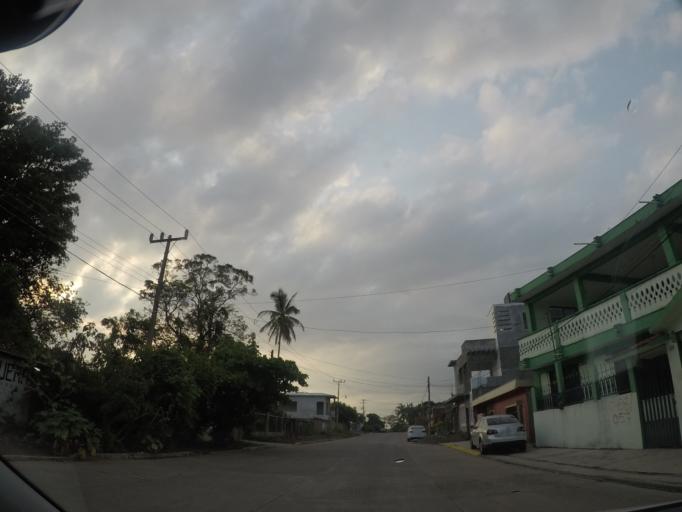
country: MX
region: Oaxaca
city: Matias Romero
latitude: 16.8723
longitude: -95.0364
